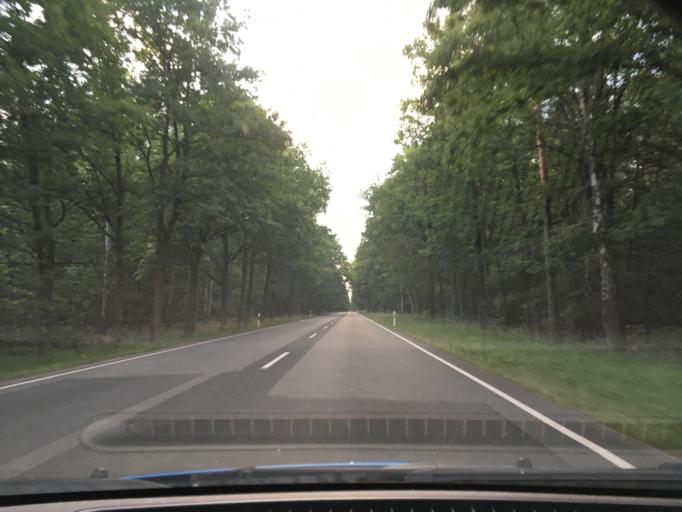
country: DE
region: Lower Saxony
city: Dedelstorf
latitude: 52.7254
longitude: 10.4836
